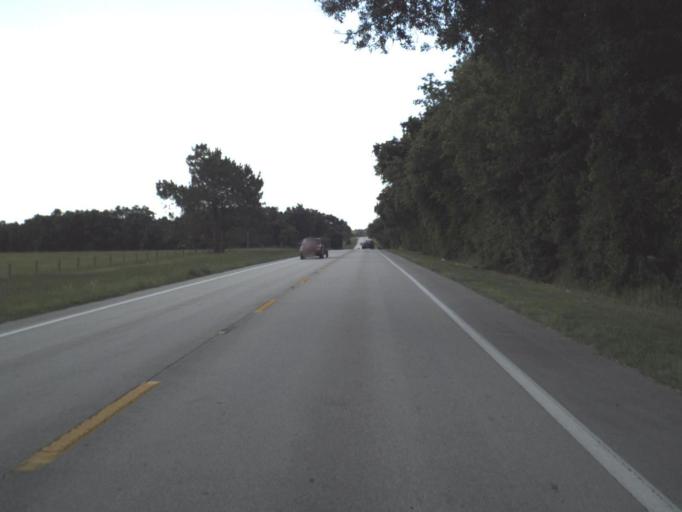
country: US
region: Florida
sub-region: Putnam County
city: Palatka
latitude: 29.5450
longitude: -81.6506
